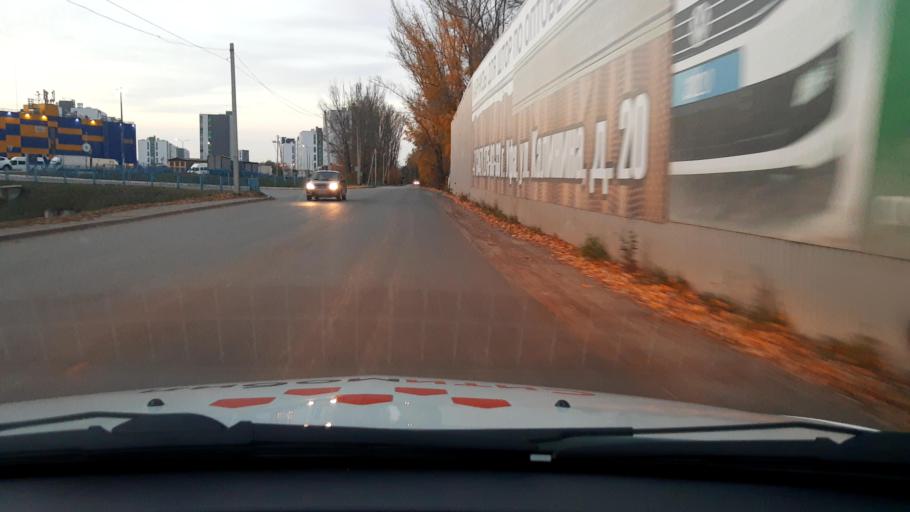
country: RU
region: Bashkortostan
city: Ufa
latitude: 54.6981
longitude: 55.9704
